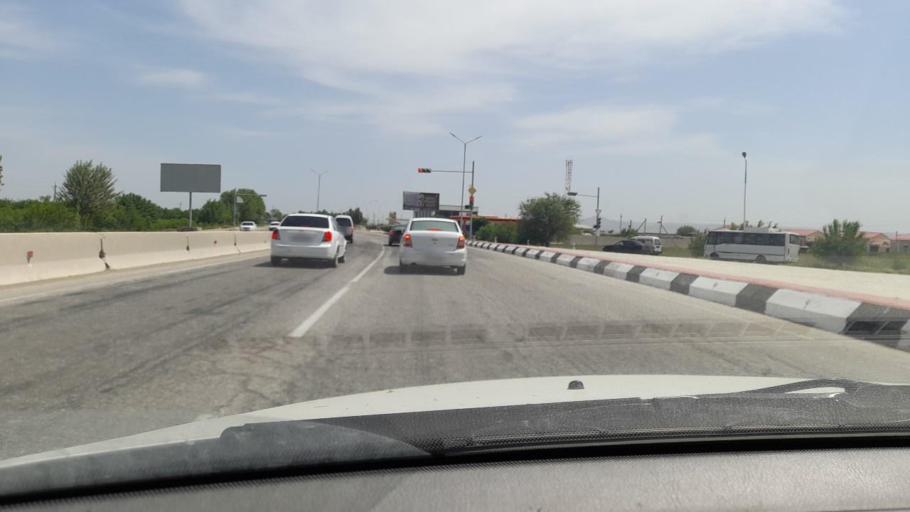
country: UZ
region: Navoiy
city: Karmana Shahri
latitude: 40.1307
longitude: 65.4097
